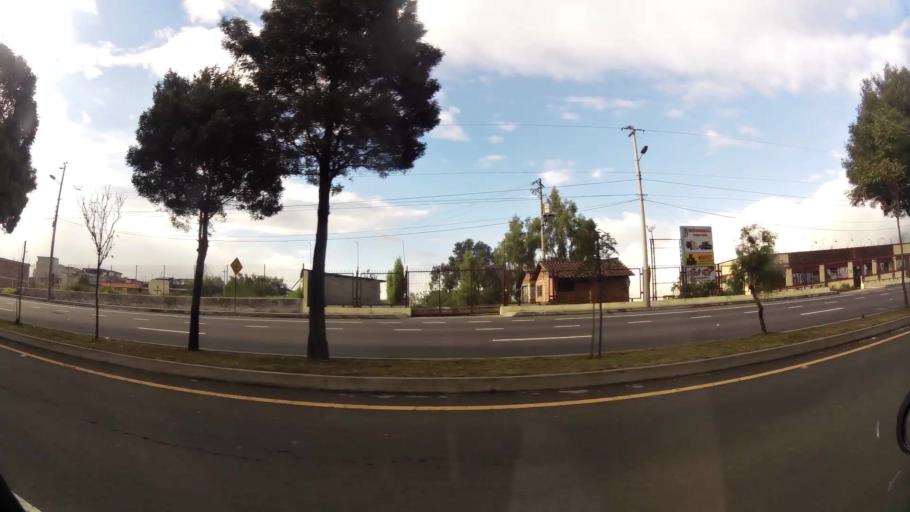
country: EC
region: Pichincha
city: Quito
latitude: -0.2318
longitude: -78.4902
